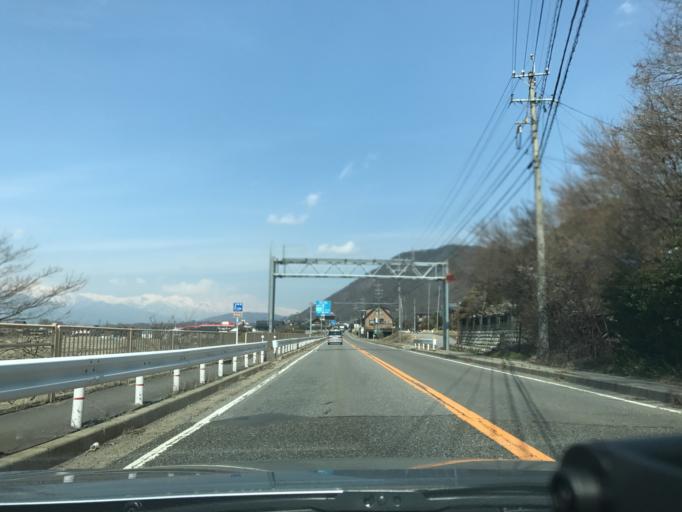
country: JP
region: Nagano
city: Toyoshina
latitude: 36.2970
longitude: 137.9412
